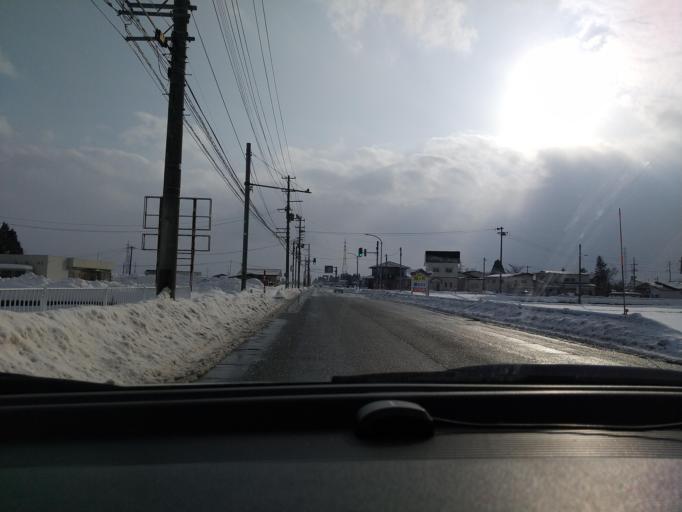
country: JP
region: Akita
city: Omagari
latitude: 39.5132
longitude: 140.5128
